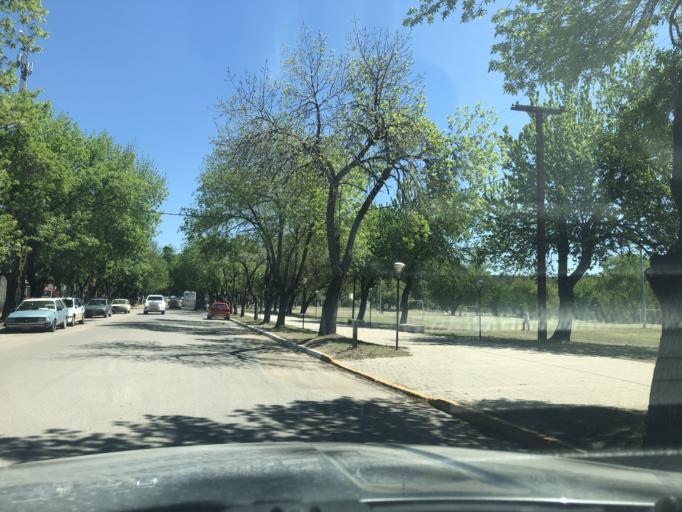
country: AR
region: Cordoba
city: La Granja
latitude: -31.0075
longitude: -64.2664
